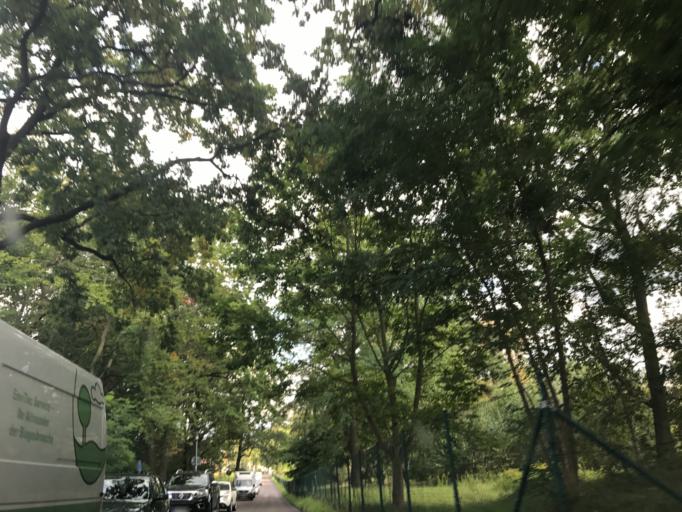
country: DE
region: Brandenburg
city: Brieselang
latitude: 52.5407
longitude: 13.0079
